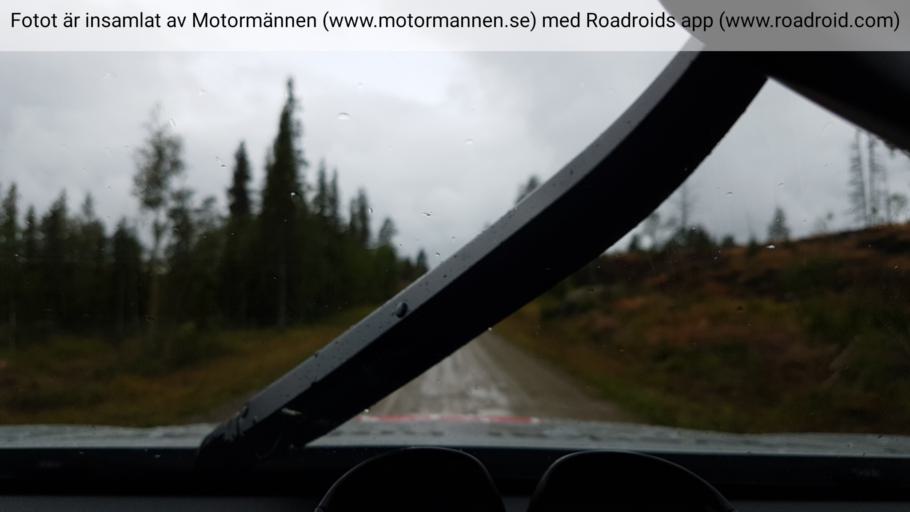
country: SE
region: Vaesterbotten
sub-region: Asele Kommun
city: Insjon
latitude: 64.7857
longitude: 17.5364
